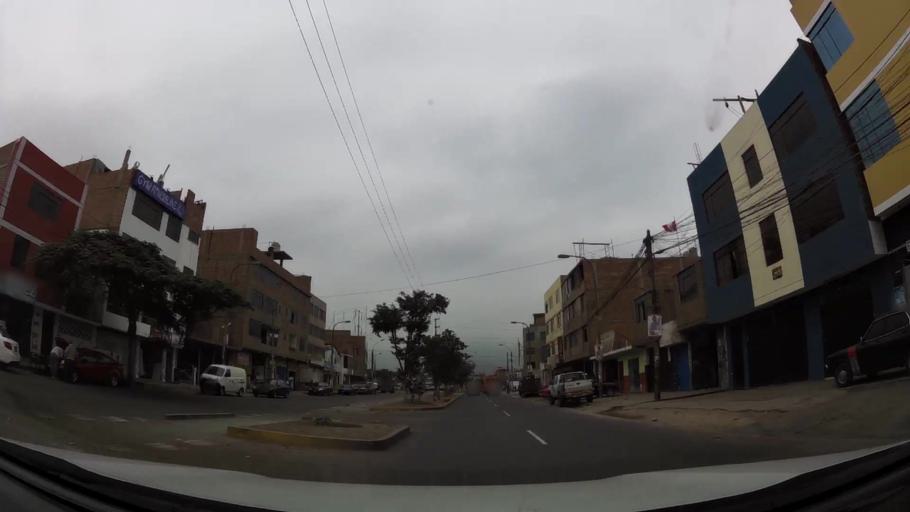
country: PE
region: Lima
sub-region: Lima
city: Independencia
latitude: -11.9831
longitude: -77.0798
